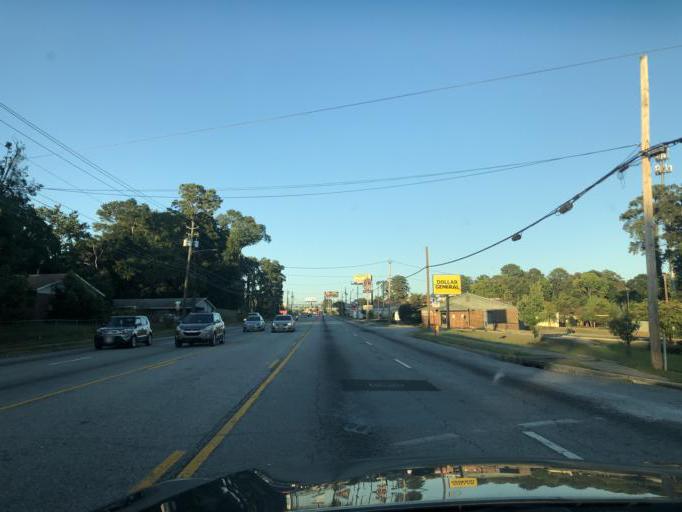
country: US
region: Georgia
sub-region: Muscogee County
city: Columbus
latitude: 32.4648
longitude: -84.9206
